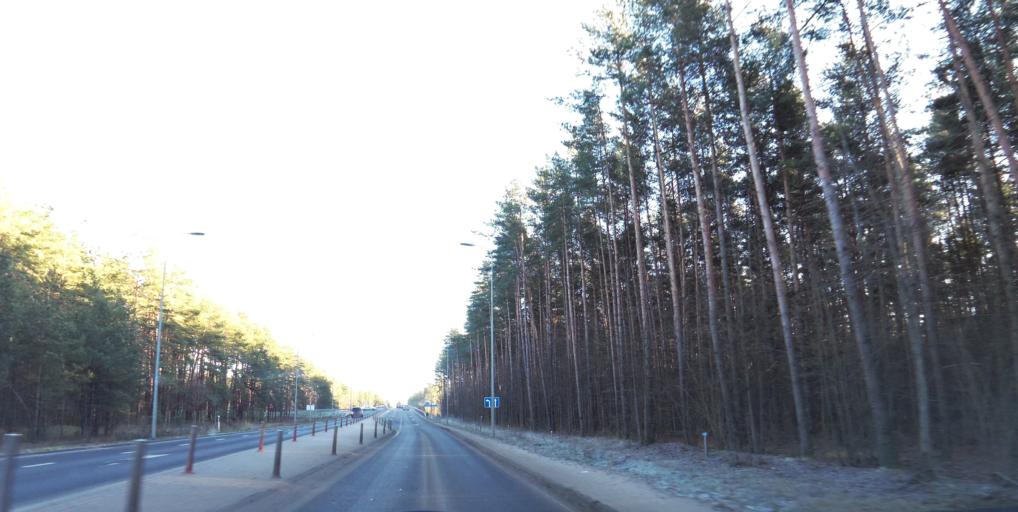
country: LT
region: Vilnius County
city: Lazdynai
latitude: 54.6451
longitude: 25.1466
